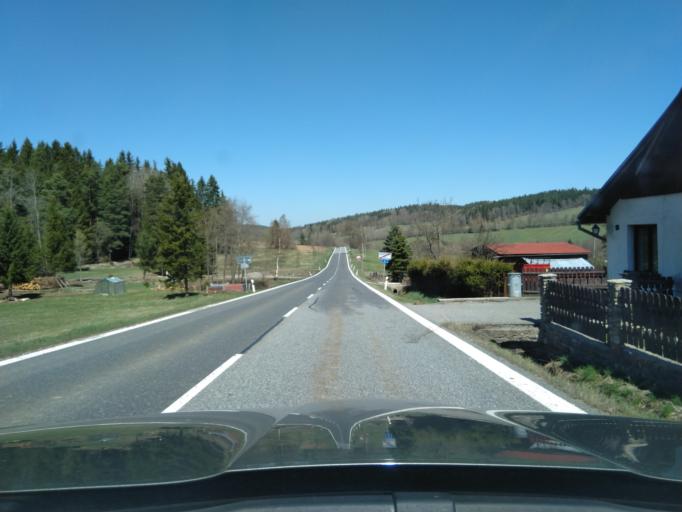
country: CZ
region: Jihocesky
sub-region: Okres Prachatice
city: Vimperk
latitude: 49.0176
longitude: 13.7689
